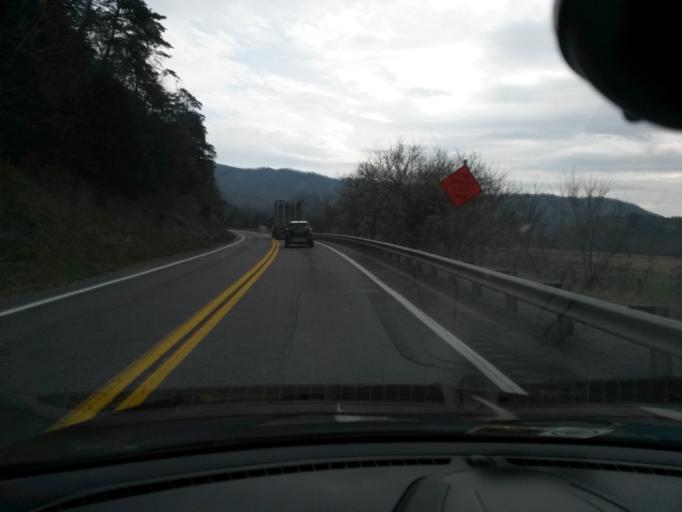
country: US
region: Virginia
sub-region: Alleghany County
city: Clifton Forge
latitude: 37.6818
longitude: -79.8060
